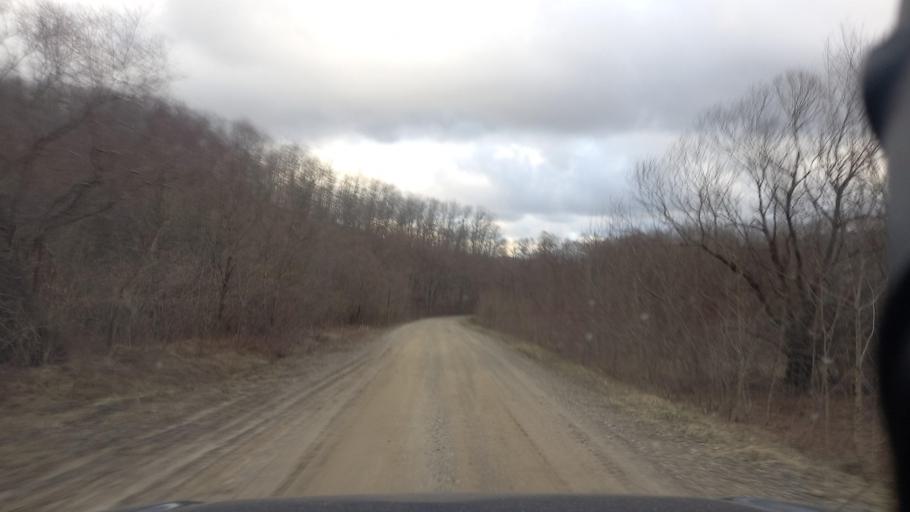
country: RU
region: Krasnodarskiy
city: Lermontovo
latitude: 44.4815
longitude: 38.7922
